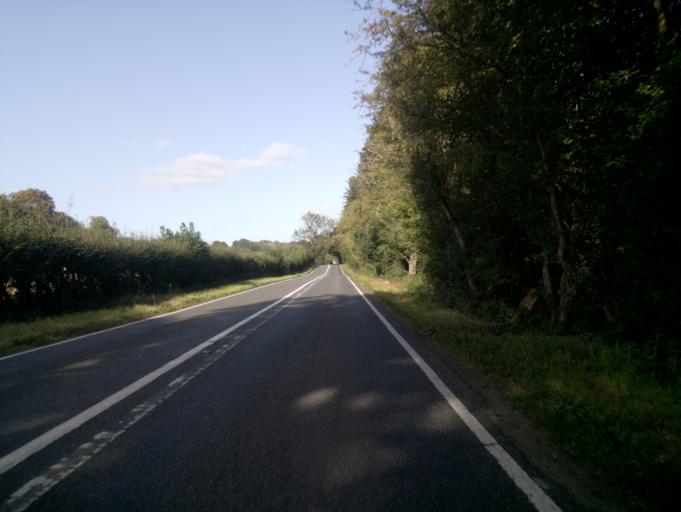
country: GB
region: England
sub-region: Hampshire
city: Four Marks
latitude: 51.0742
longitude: -1.0134
